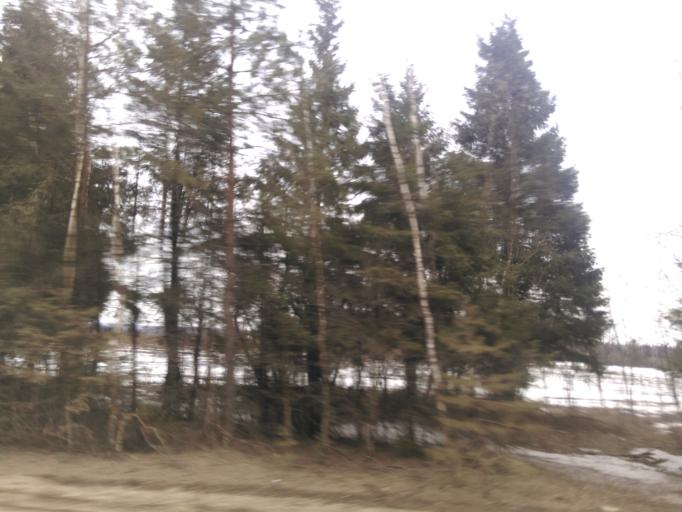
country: RU
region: Moskovskaya
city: Kolyubakino
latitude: 55.6329
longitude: 36.5385
